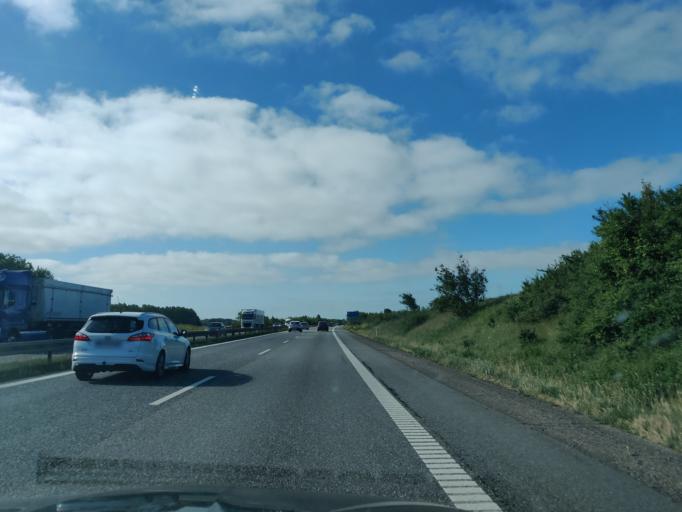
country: DK
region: North Denmark
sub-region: Mariagerfjord Kommune
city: Hobro
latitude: 56.6828
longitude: 9.7316
